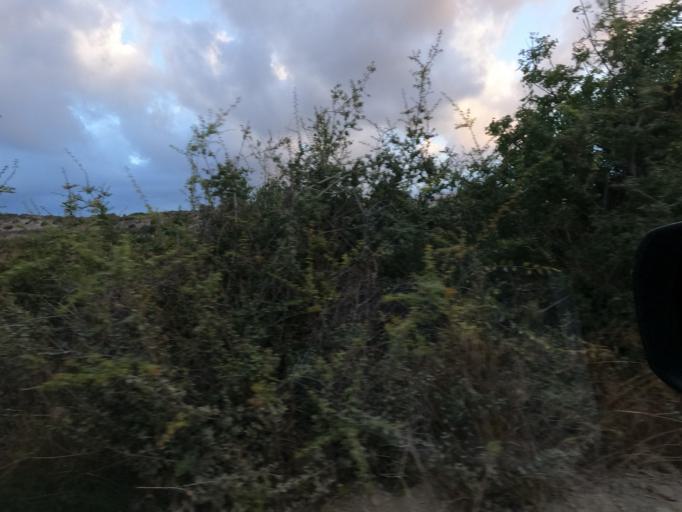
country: CY
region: Pafos
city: Mesogi
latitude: 34.8483
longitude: 32.5343
